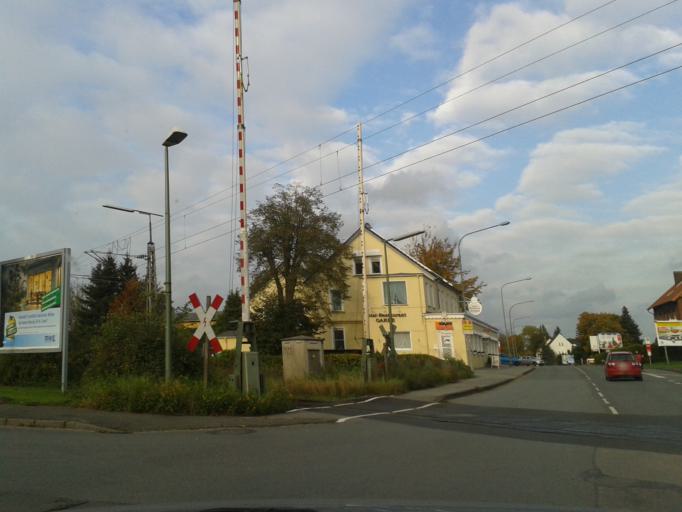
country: DE
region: North Rhine-Westphalia
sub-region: Regierungsbezirk Detmold
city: Horn-Bad Meinberg
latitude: 51.8799
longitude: 8.9555
